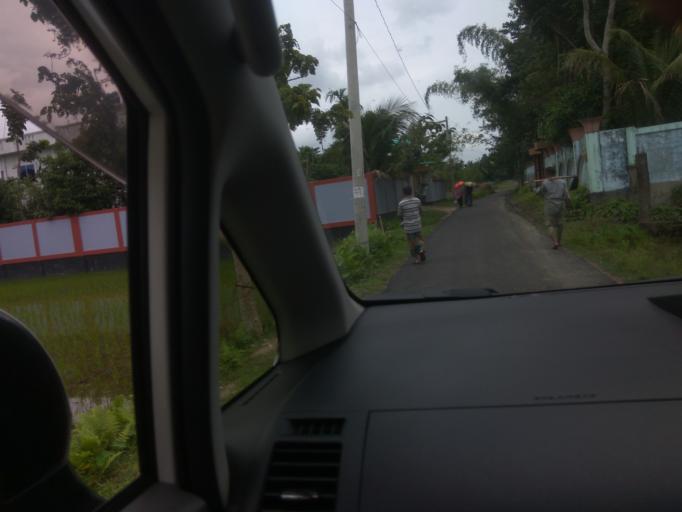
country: IN
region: Assam
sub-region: Karimganj
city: Karimganj
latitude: 24.8508
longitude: 92.1424
